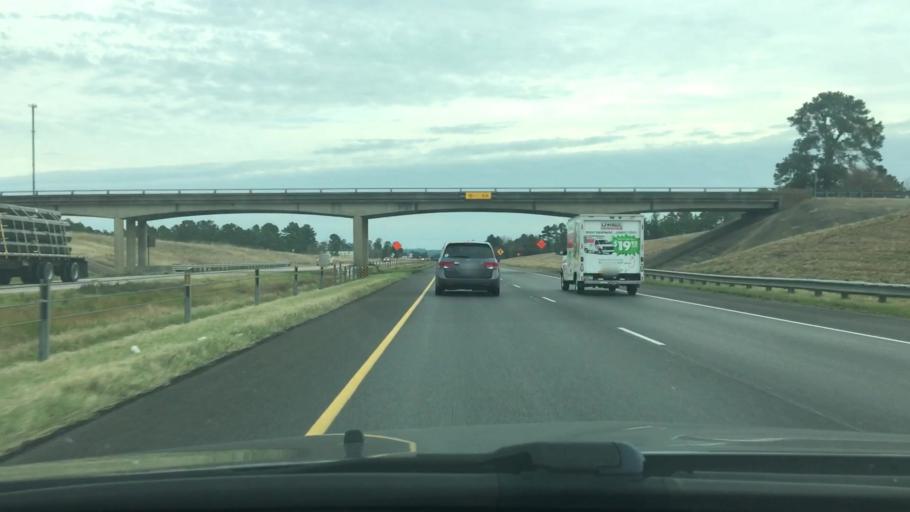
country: US
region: Texas
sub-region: Madison County
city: Madisonville
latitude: 30.8740
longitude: -95.7609
